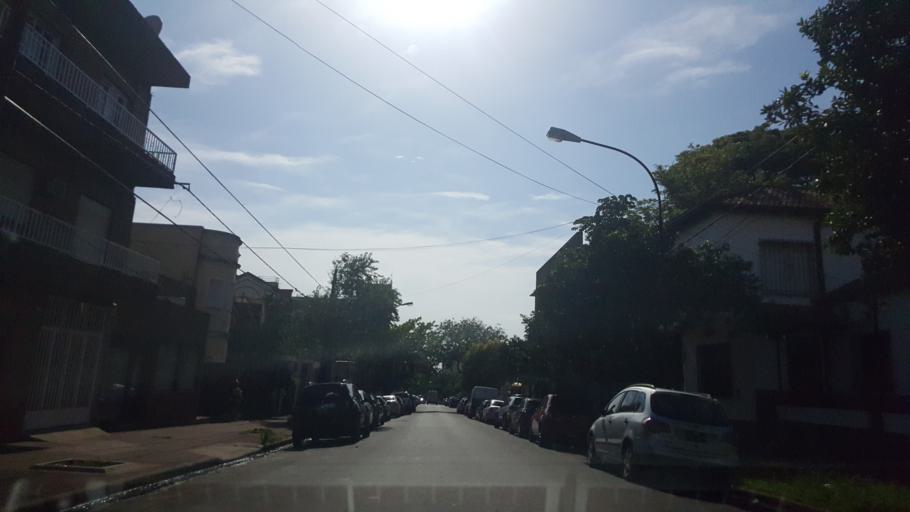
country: AR
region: Misiones
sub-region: Departamento de Capital
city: Posadas
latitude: -27.3734
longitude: -55.8954
